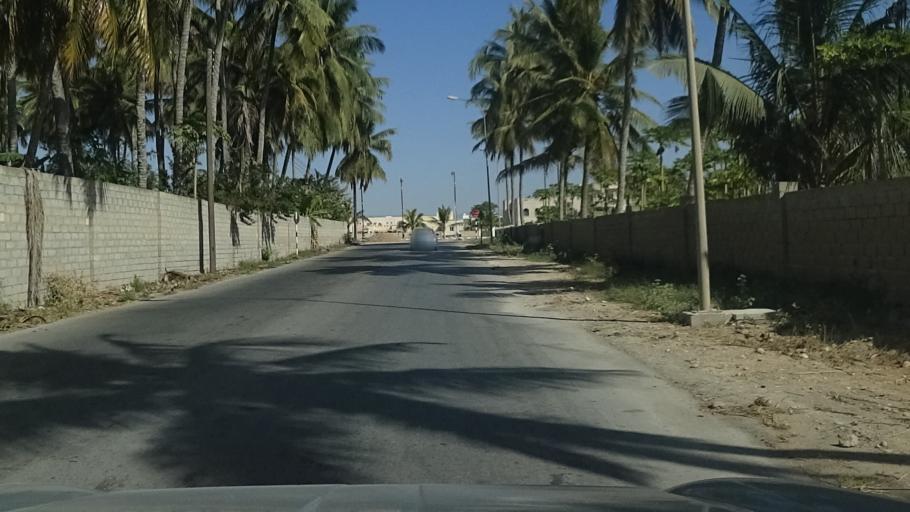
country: OM
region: Zufar
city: Salalah
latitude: 17.0350
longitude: 54.1578
